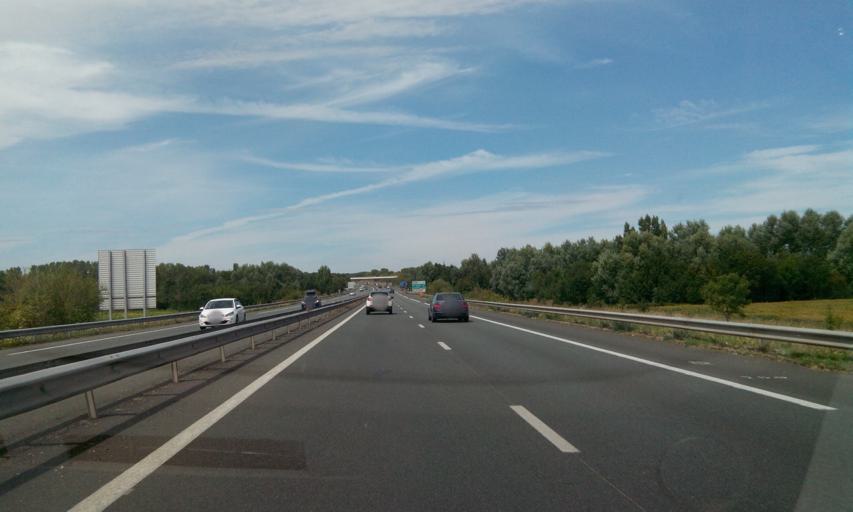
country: FR
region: Pays de la Loire
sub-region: Departement de la Vendee
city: Sainte-Hermine
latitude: 46.5425
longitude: -1.0837
